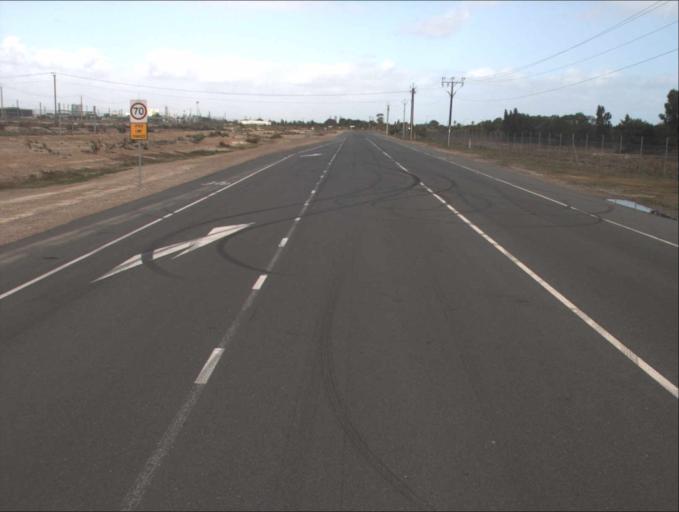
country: AU
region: South Australia
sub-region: Port Adelaide Enfield
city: Birkenhead
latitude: -34.7766
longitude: 138.5016
